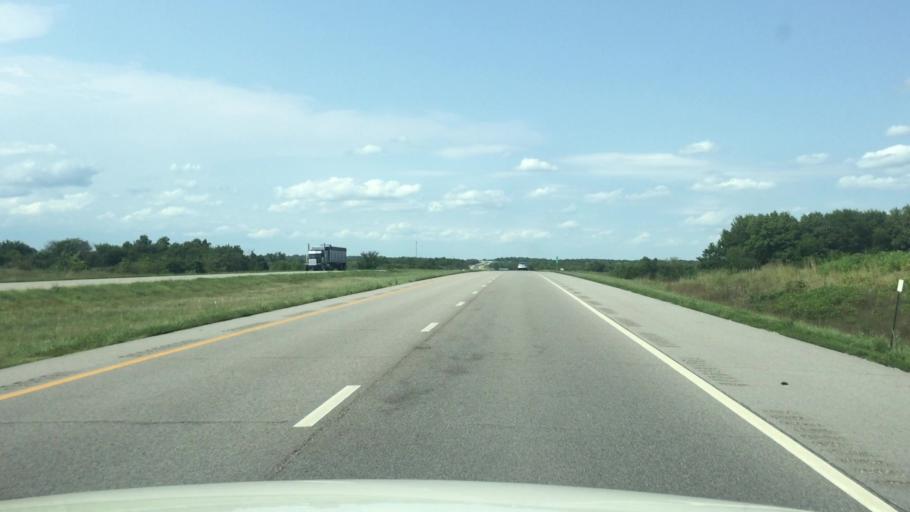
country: US
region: Kansas
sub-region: Linn County
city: La Cygne
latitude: 38.4382
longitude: -94.6865
